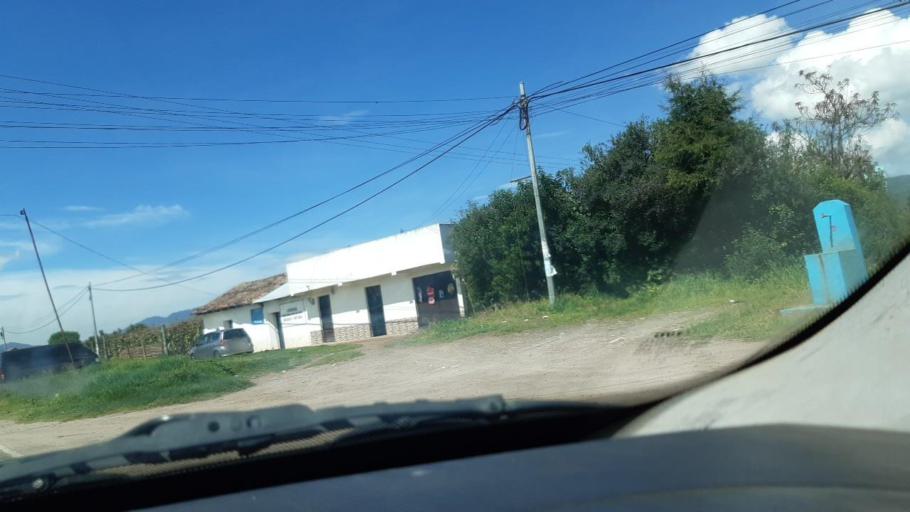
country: GT
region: Quetzaltenango
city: Salcaja
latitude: 14.8804
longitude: -91.4465
